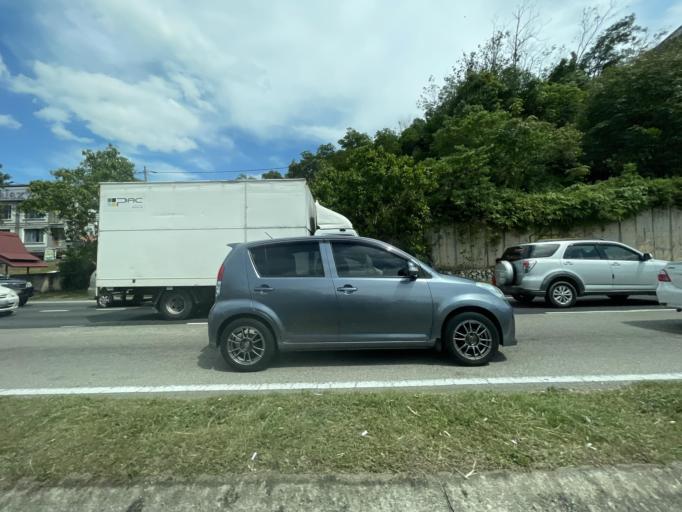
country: MY
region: Melaka
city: Batu Berendam
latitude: 2.2477
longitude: 102.2231
